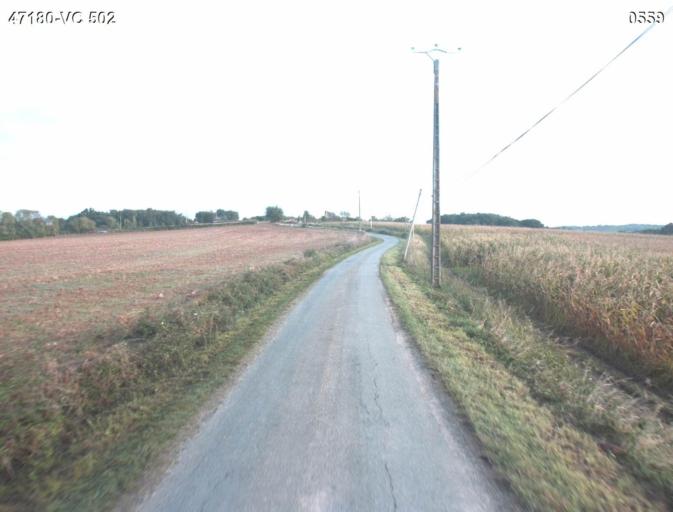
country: FR
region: Aquitaine
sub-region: Departement du Lot-et-Garonne
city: Sainte-Colombe-en-Bruilhois
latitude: 44.1632
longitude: 0.4805
